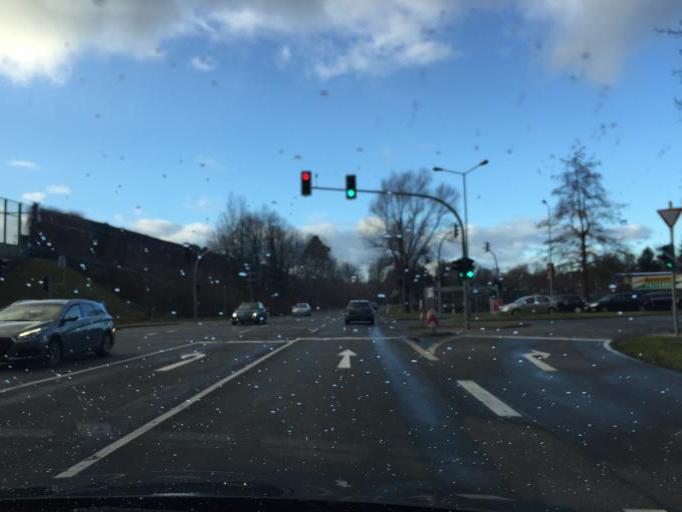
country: DE
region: Brandenburg
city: Vetschau
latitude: 51.7793
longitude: 14.0742
